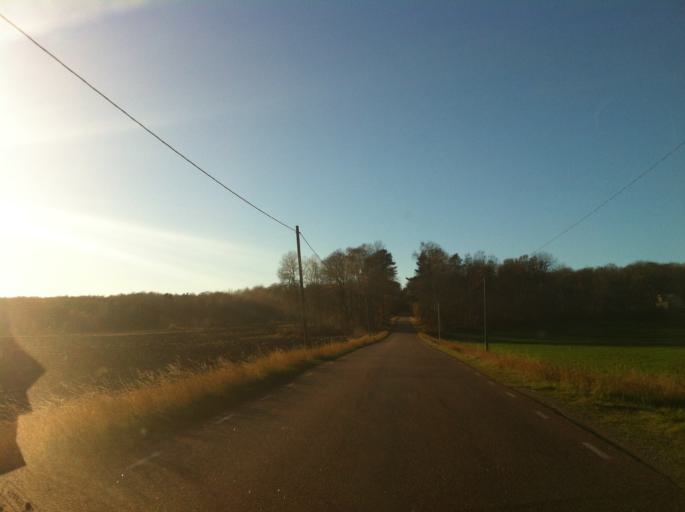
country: SE
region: Blekinge
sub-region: Olofstroms Kommun
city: Jamshog
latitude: 56.1870
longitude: 14.6051
